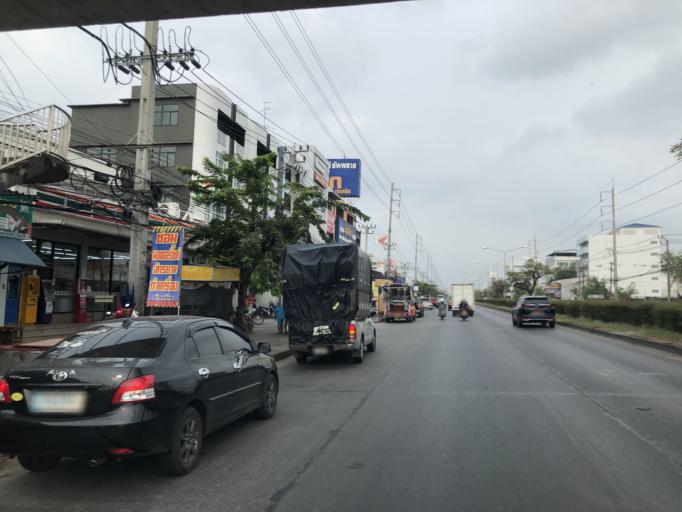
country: TH
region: Bangkok
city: Bang Na
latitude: 13.6081
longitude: 100.6832
